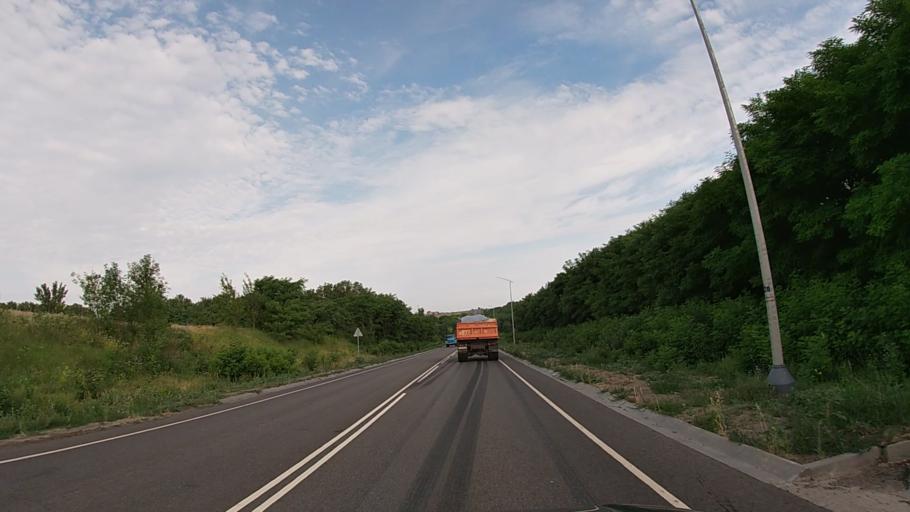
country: RU
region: Belgorod
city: Severnyy
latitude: 50.6670
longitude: 36.4940
